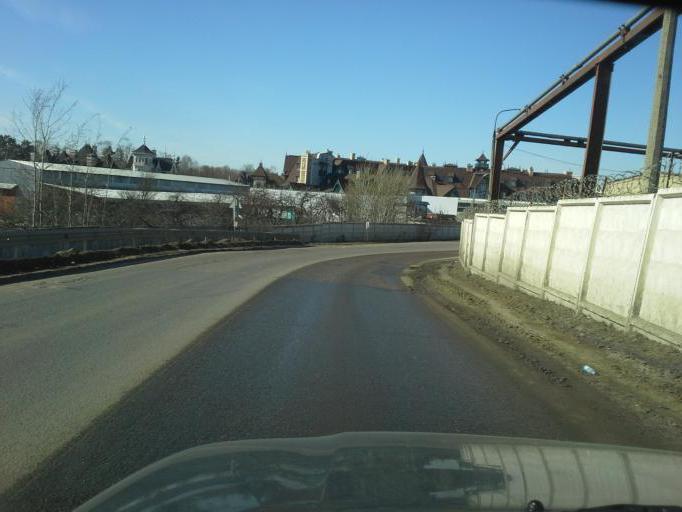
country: RU
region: Moskovskaya
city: Odintsovo
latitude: 55.6563
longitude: 37.2549
